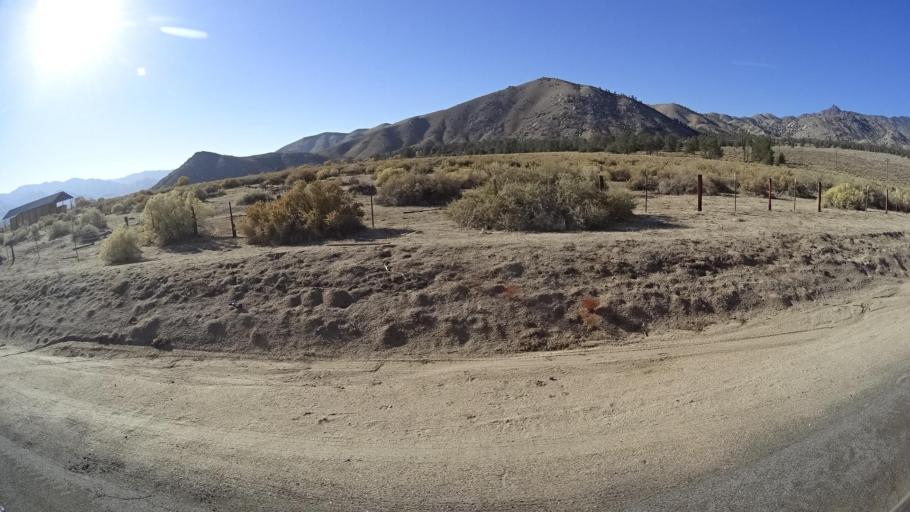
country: US
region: California
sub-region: Kern County
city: Weldon
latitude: 35.6892
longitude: -118.2886
